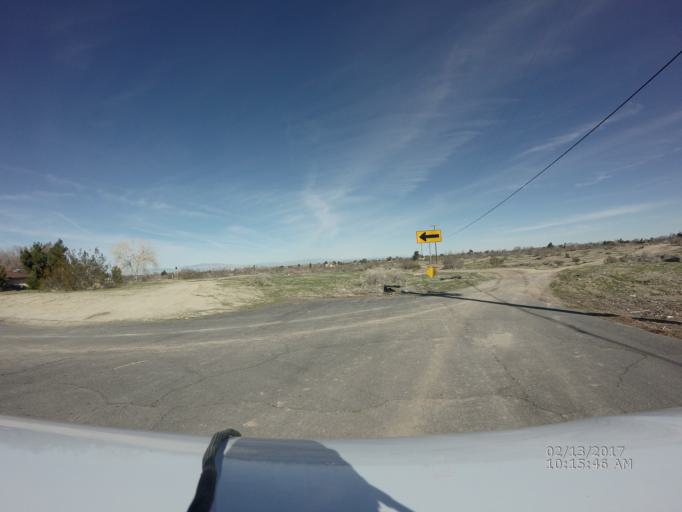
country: US
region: California
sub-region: Los Angeles County
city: Littlerock
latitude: 34.5243
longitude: -117.9713
